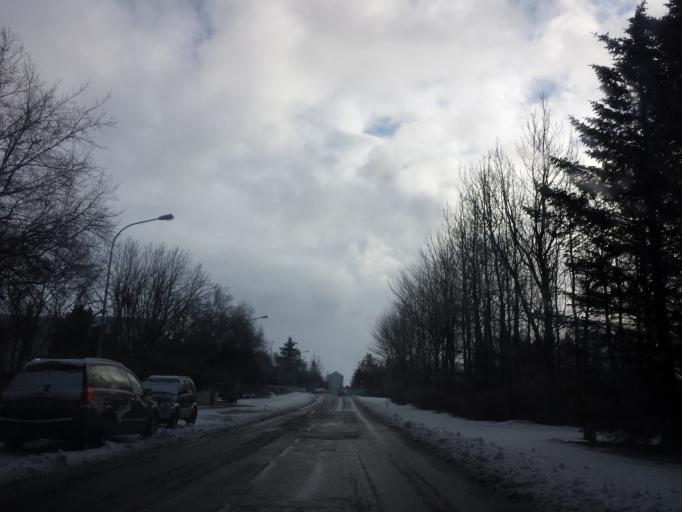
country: IS
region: Capital Region
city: Reykjavik
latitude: 64.1382
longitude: -21.9111
